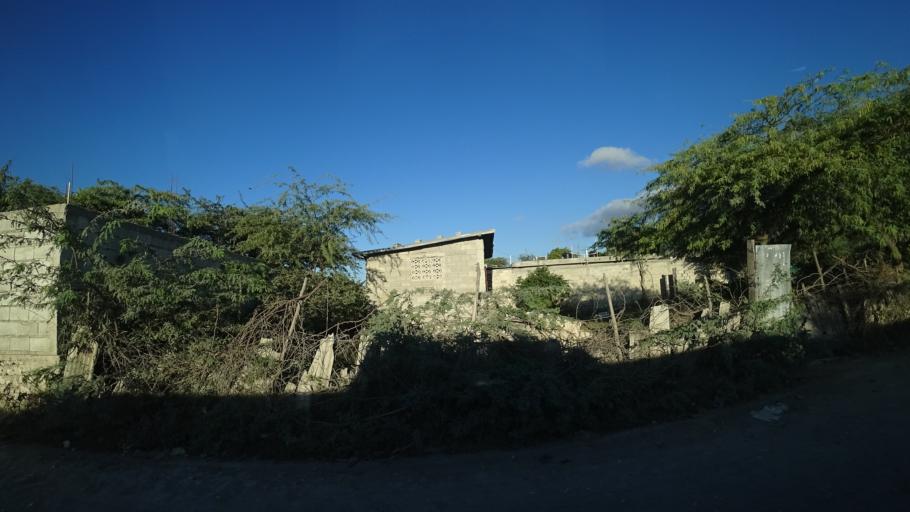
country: HT
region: Ouest
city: Croix des Bouquets
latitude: 18.6499
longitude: -72.2568
